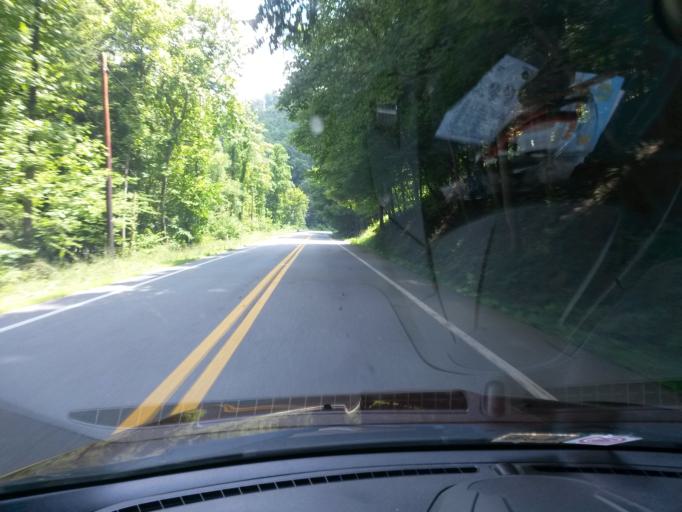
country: US
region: West Virginia
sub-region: Wyoming County
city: Pineville
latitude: 37.5510
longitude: -81.5706
